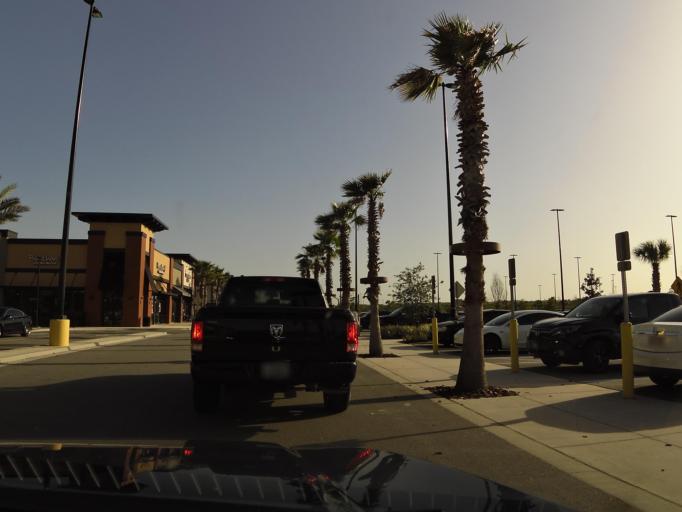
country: US
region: Florida
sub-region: Saint Johns County
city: Fruit Cove
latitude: 30.0984
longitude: -81.5194
